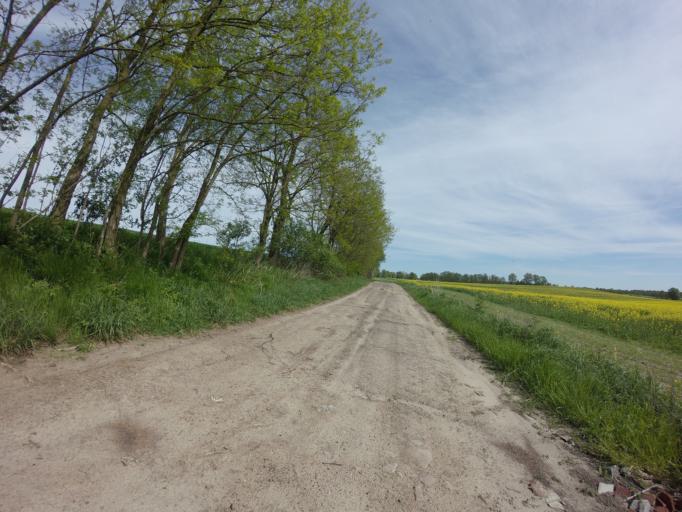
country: PL
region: West Pomeranian Voivodeship
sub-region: Powiat choszczenski
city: Recz
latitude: 53.1727
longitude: 15.5588
